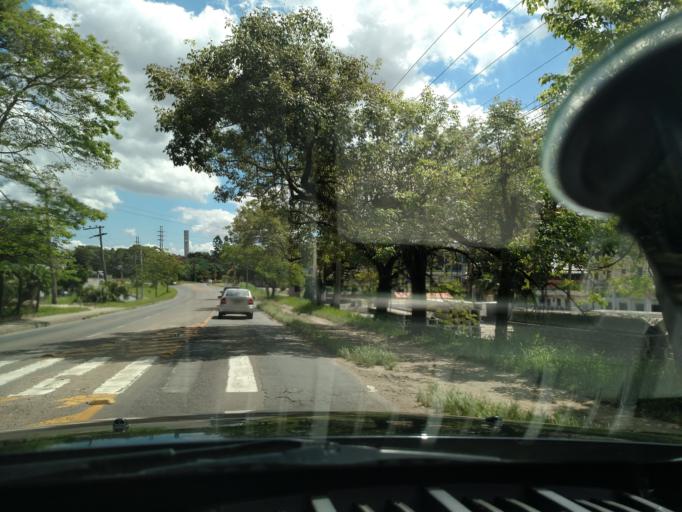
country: BR
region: Santa Catarina
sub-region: Blumenau
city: Blumenau
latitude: -26.8733
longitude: -49.1040
